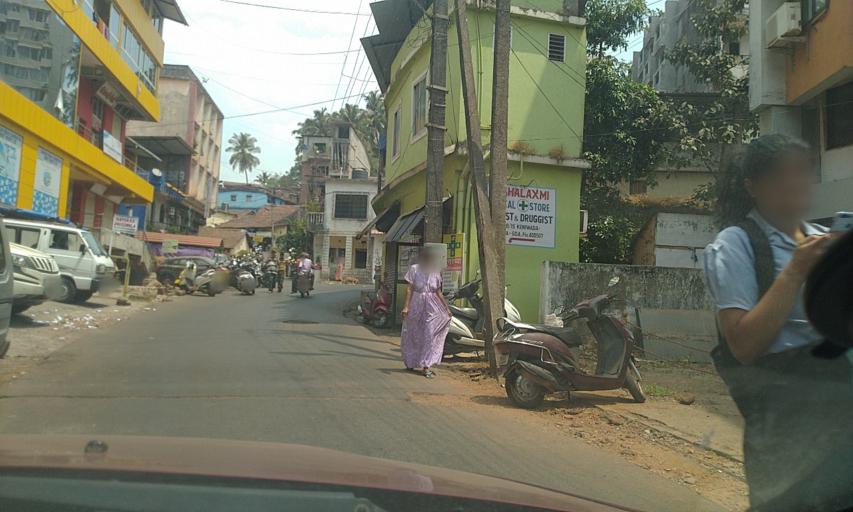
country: IN
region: Goa
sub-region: North Goa
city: Mapuca
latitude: 15.5916
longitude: 73.8106
